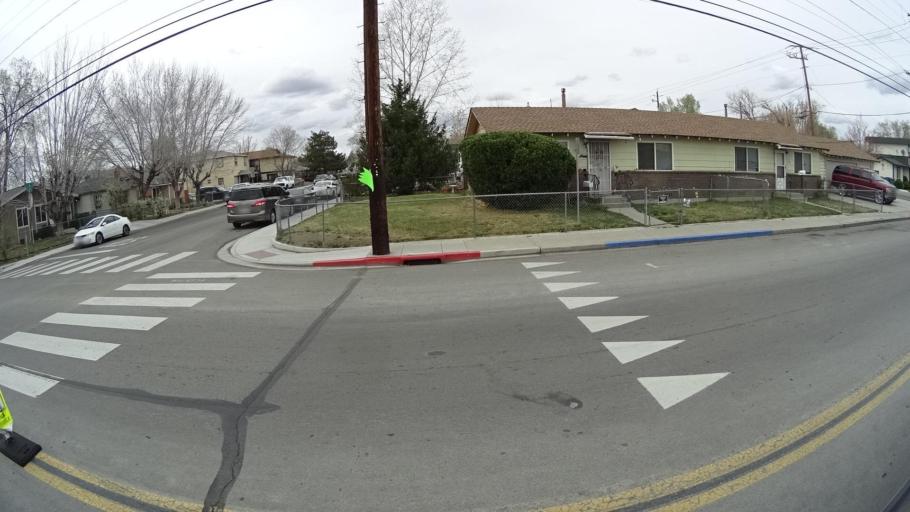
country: US
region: Nevada
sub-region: Washoe County
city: Sparks
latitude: 39.5398
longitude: -119.7621
